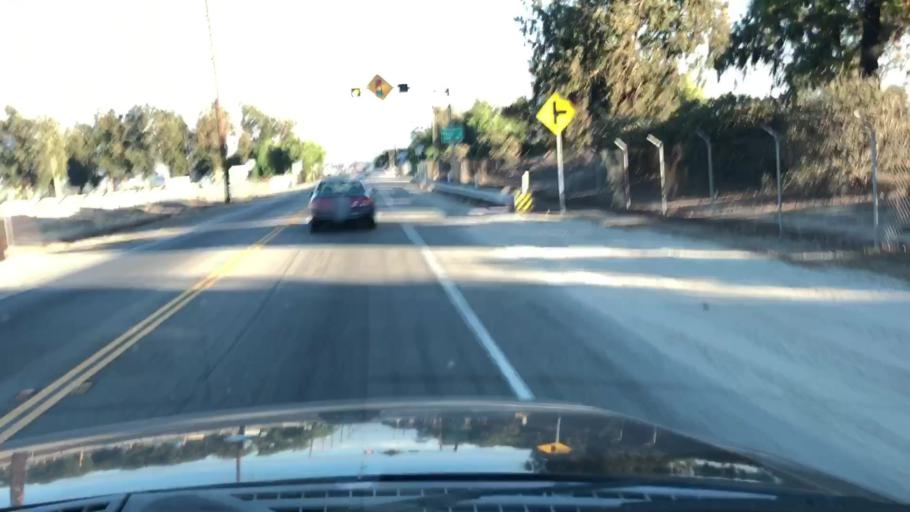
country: US
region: California
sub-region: Ventura County
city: Saticoy
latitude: 34.2694
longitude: -119.1287
